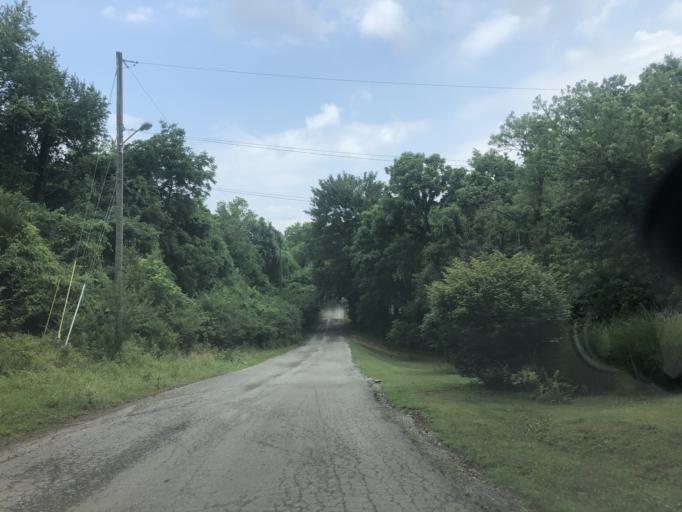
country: US
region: Tennessee
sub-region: Davidson County
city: Lakewood
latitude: 36.2233
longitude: -86.6292
